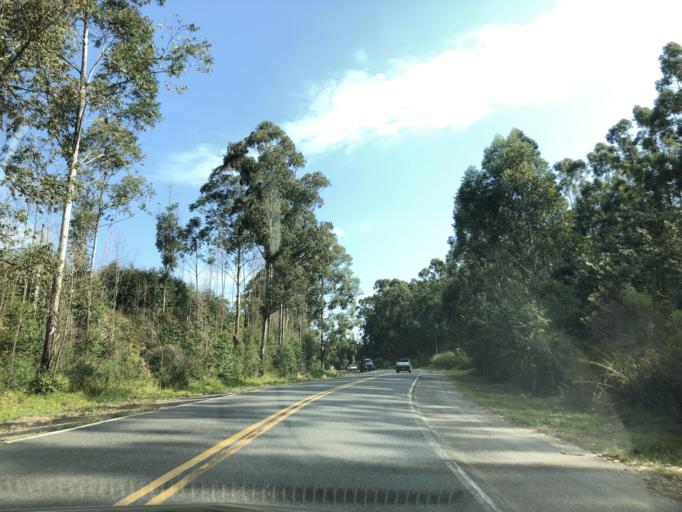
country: BR
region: Sao Paulo
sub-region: Pilar Do Sul
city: Pilar do Sul
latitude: -23.8150
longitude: -47.6469
